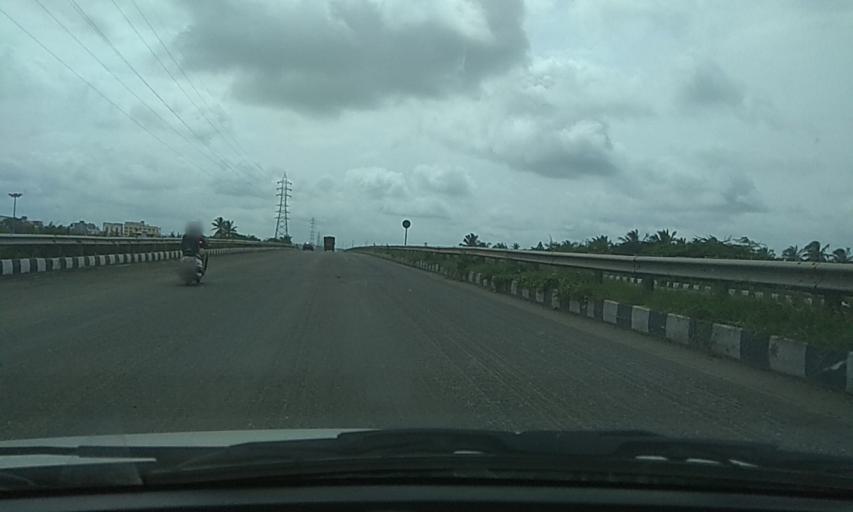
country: IN
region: Karnataka
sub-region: Davanagere
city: Harihar
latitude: 14.4420
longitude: 75.8978
